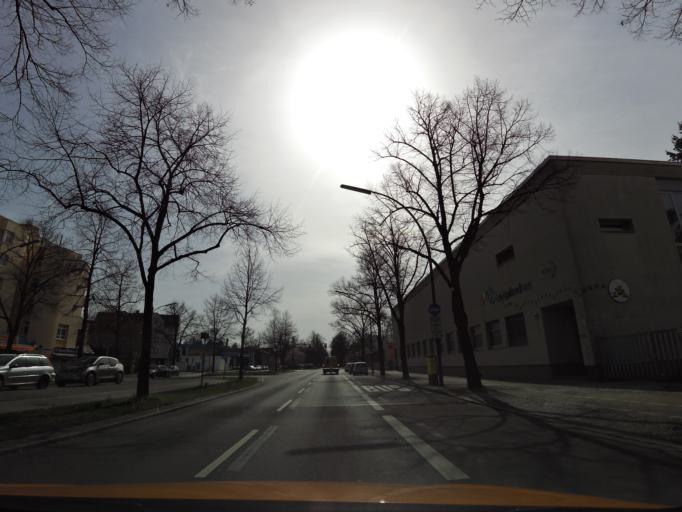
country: DE
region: Berlin
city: Mariendorf
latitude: 52.4241
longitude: 13.3956
